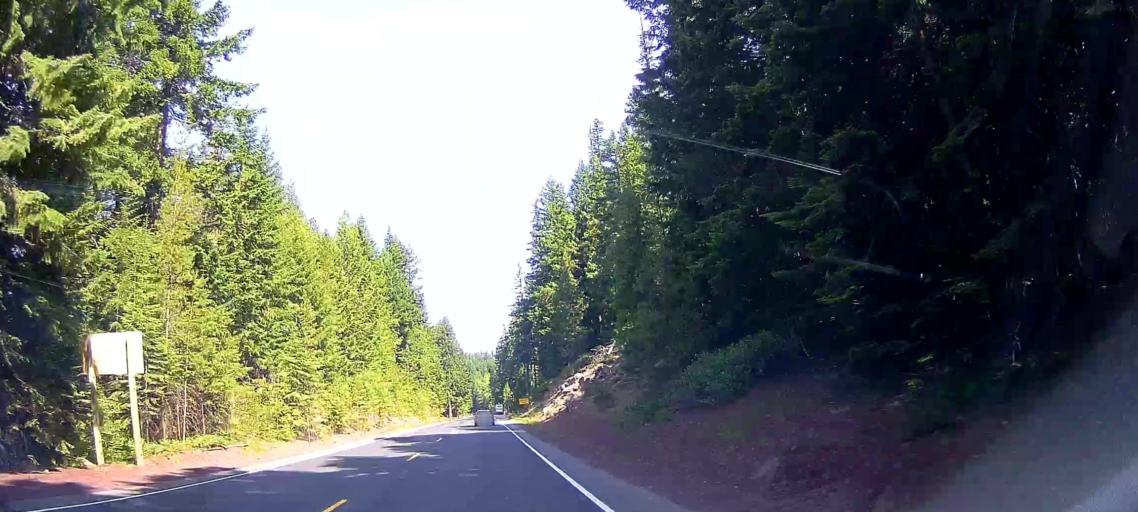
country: US
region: Oregon
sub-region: Clackamas County
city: Mount Hood Village
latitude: 45.1220
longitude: -121.5844
